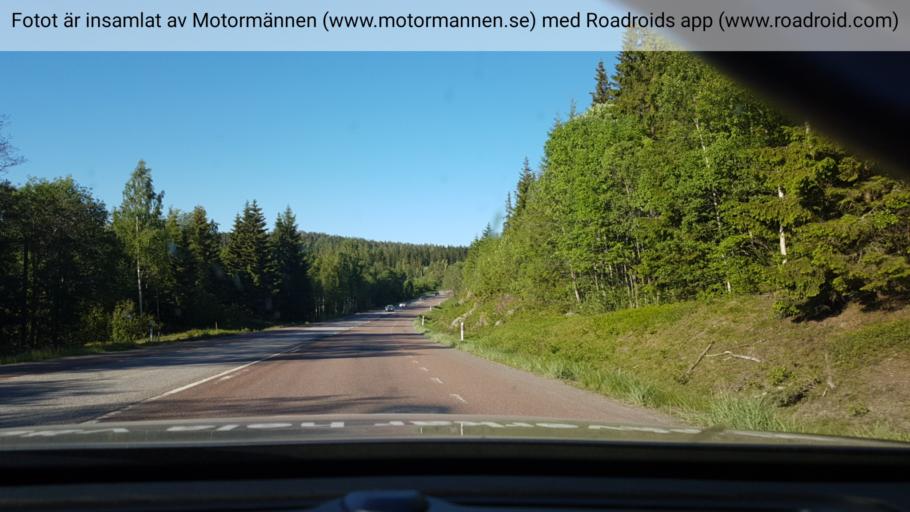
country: SE
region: Vaesternorrland
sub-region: Haernoesands Kommun
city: Haernoesand
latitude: 62.7021
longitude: 17.8579
